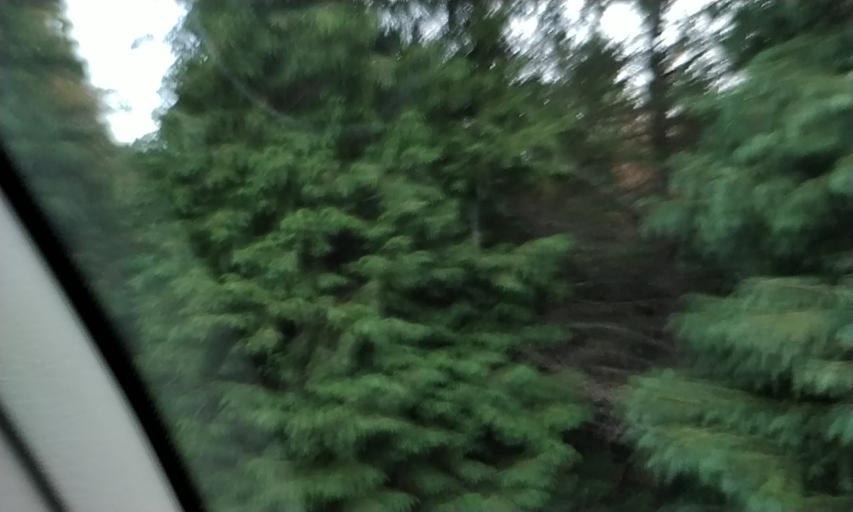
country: PT
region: Vila Real
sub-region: Vila Real
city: Vila Real
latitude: 41.3032
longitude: -7.7768
